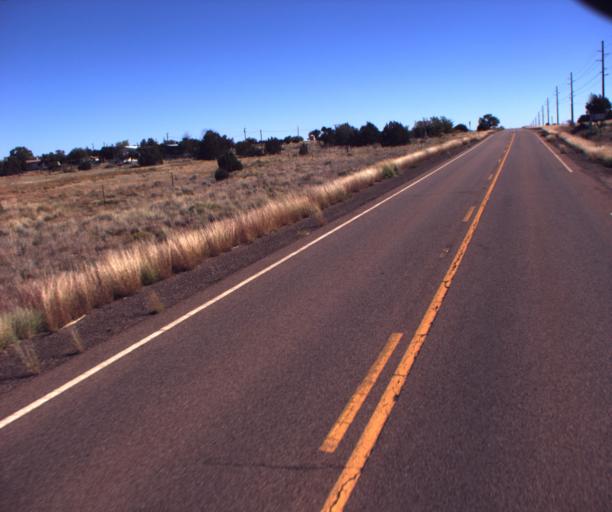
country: US
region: Arizona
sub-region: Navajo County
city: Taylor
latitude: 34.4843
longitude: -110.2559
